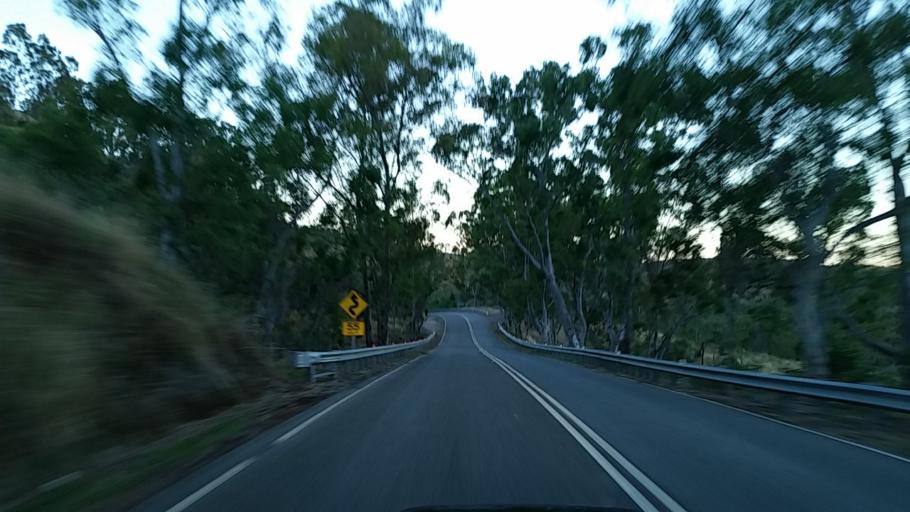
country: AU
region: South Australia
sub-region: Campbelltown
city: Athelstone
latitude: -34.8566
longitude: 138.7905
